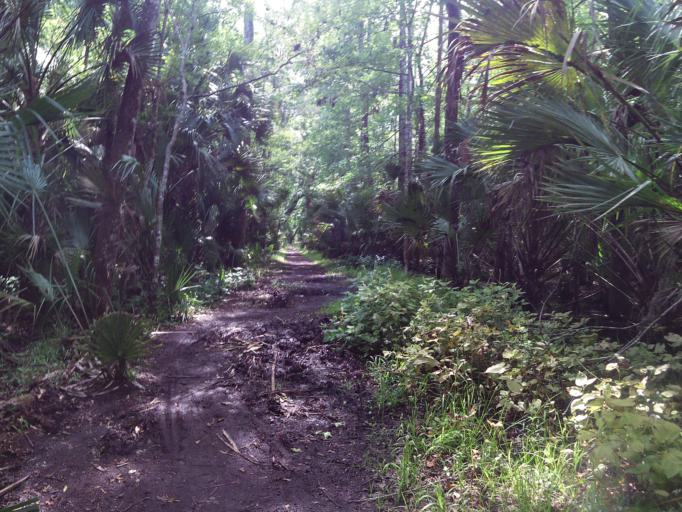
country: US
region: Florida
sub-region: Flagler County
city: Flagler Beach
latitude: 29.3974
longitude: -81.1306
